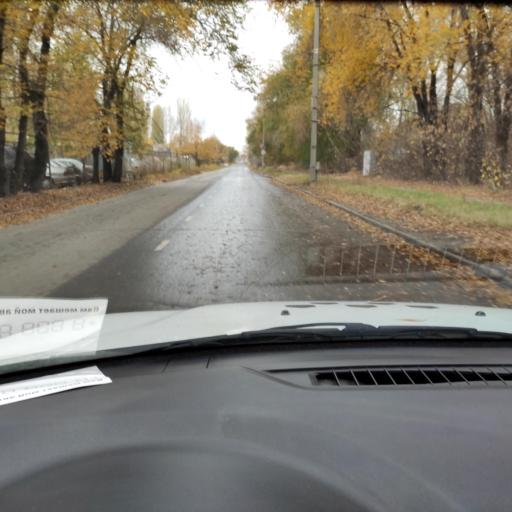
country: RU
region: Samara
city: Tol'yatti
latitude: 53.5532
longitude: 49.3087
